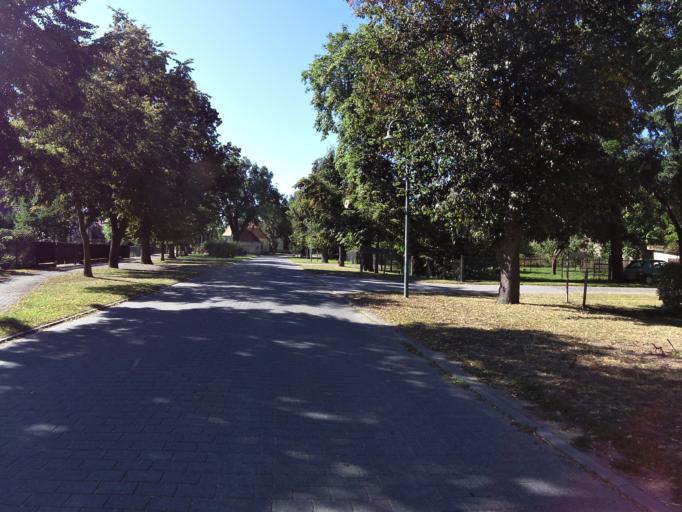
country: DE
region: Saxony
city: Elsnig
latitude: 51.6143
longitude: 12.9690
